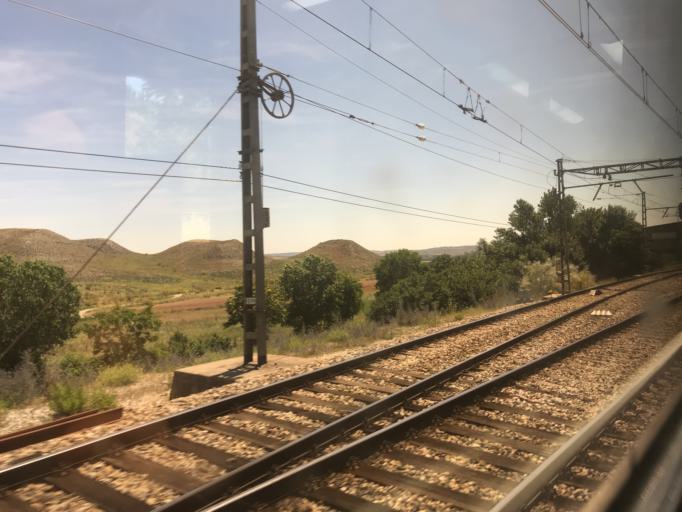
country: ES
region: Madrid
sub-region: Provincia de Madrid
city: Ciempozuelos
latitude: 40.1641
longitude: -3.6121
